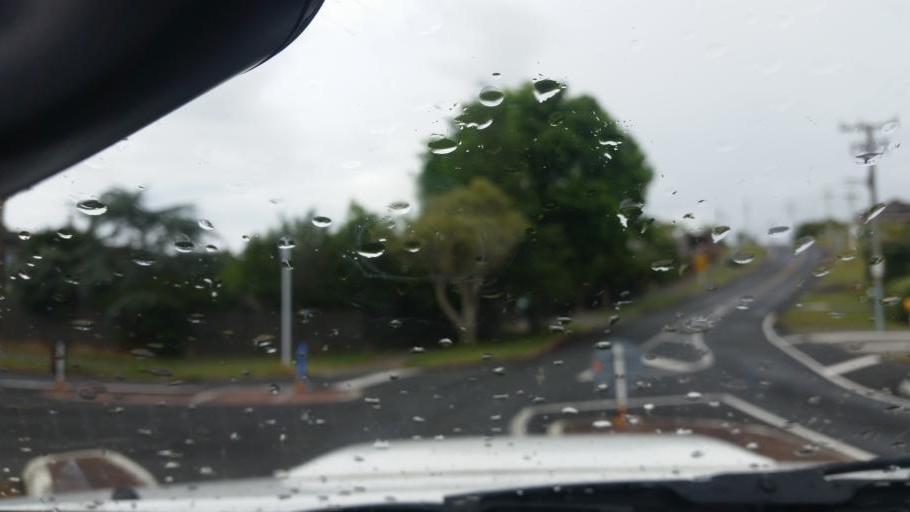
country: NZ
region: Northland
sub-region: Kaipara District
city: Dargaville
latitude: -35.9299
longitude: 173.8631
